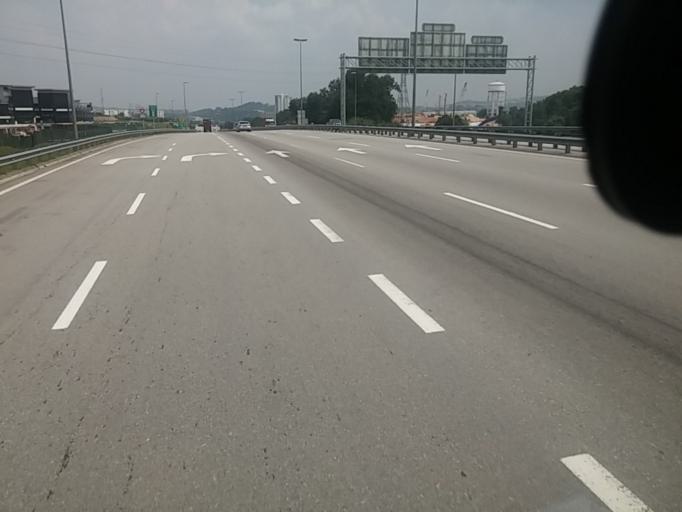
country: MY
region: Putrajaya
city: Putrajaya
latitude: 2.9741
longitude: 101.6614
